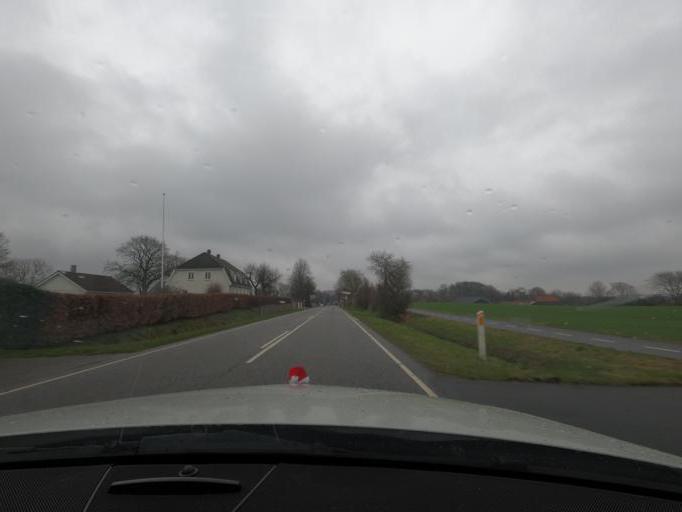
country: DK
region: South Denmark
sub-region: Haderslev Kommune
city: Starup
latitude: 55.2536
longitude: 9.6324
